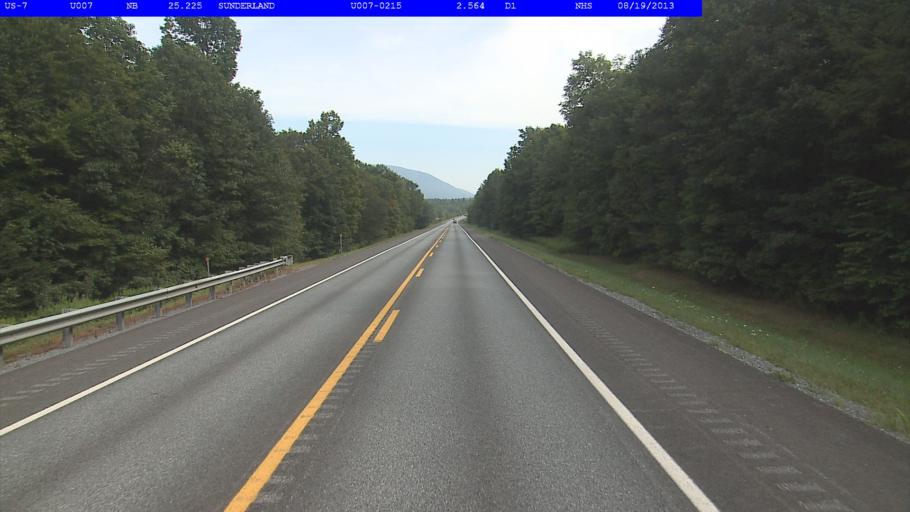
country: US
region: Vermont
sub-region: Bennington County
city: Arlington
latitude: 43.0612
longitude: -73.1249
